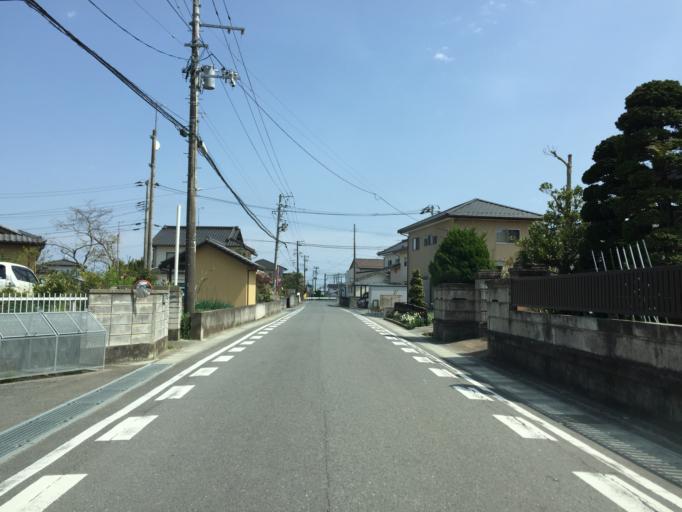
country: JP
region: Fukushima
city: Iwaki
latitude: 37.1420
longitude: 140.9939
